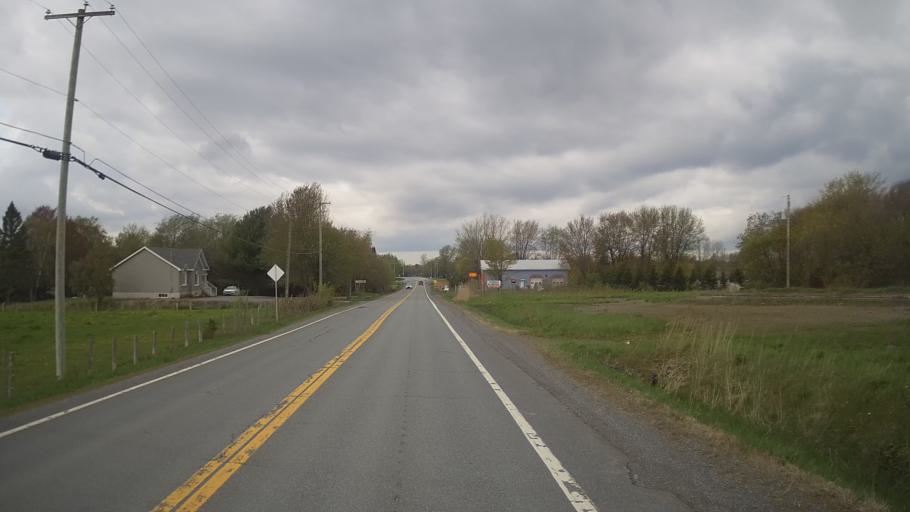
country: CA
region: Quebec
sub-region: Monteregie
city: Farnham
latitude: 45.2681
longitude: -72.9438
